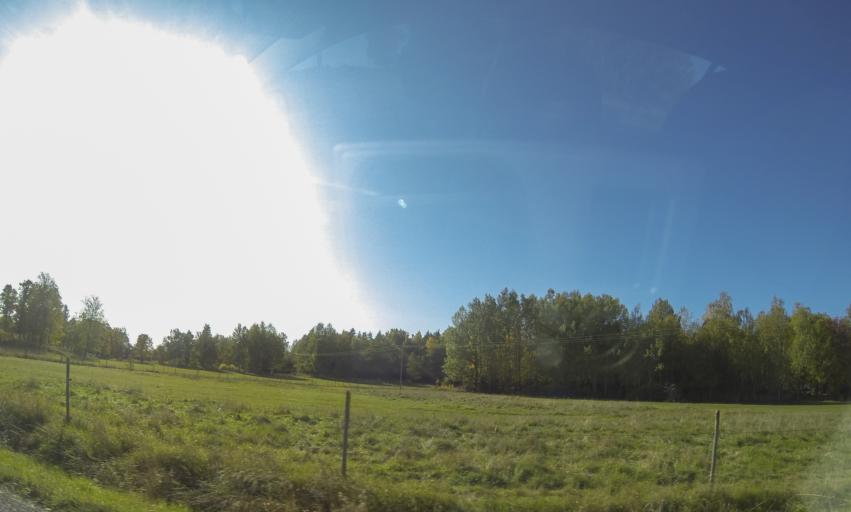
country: SE
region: Soedermanland
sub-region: Eskilstuna Kommun
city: Kvicksund
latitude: 59.5160
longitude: 16.3399
